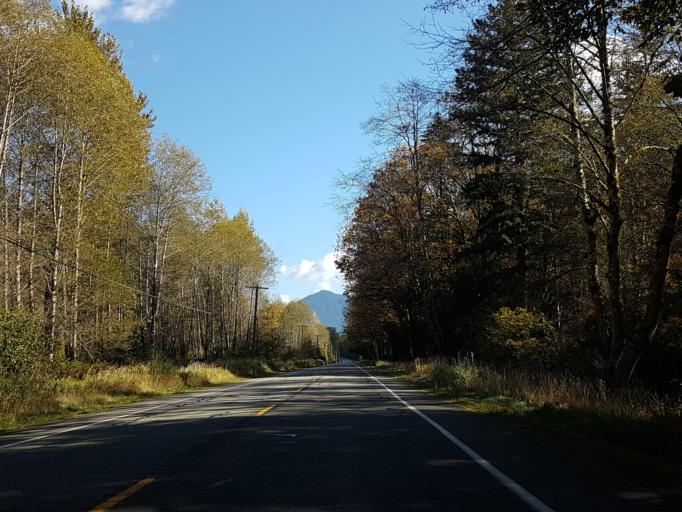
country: US
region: Washington
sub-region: Snohomish County
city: Gold Bar
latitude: 47.7602
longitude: -121.4699
